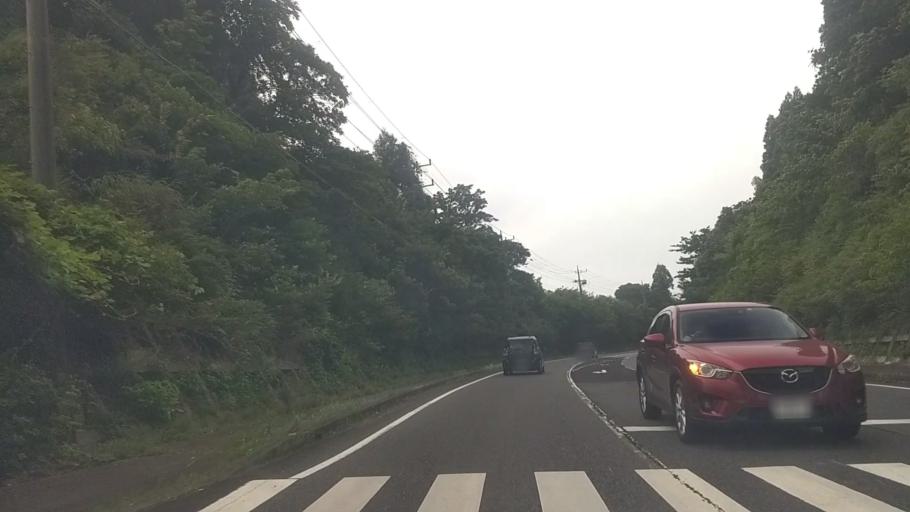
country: JP
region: Chiba
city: Ohara
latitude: 35.2729
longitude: 140.2521
